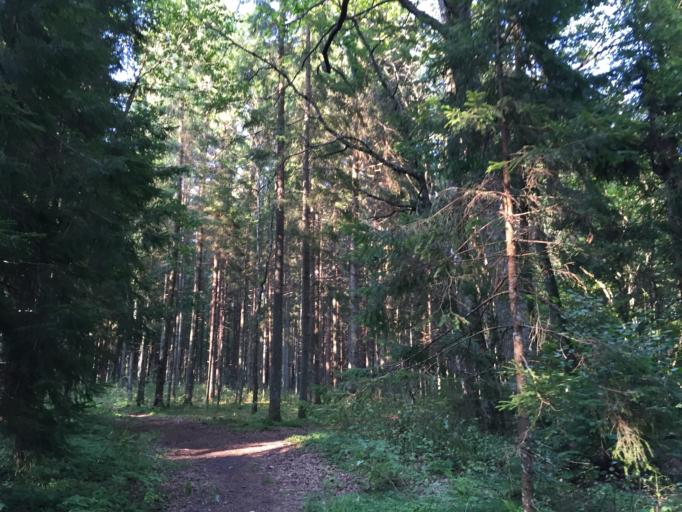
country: LV
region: Limbazu Rajons
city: Limbazi
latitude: 57.5648
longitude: 24.8005
